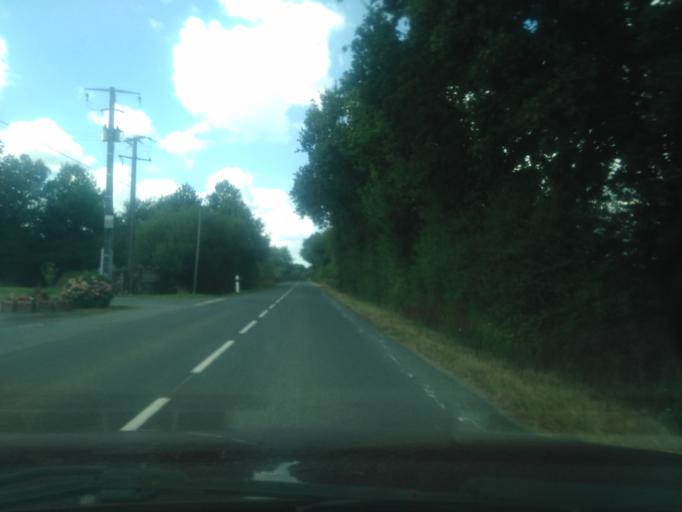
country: FR
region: Pays de la Loire
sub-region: Departement de la Vendee
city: Chauche
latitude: 46.8403
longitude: -1.2873
